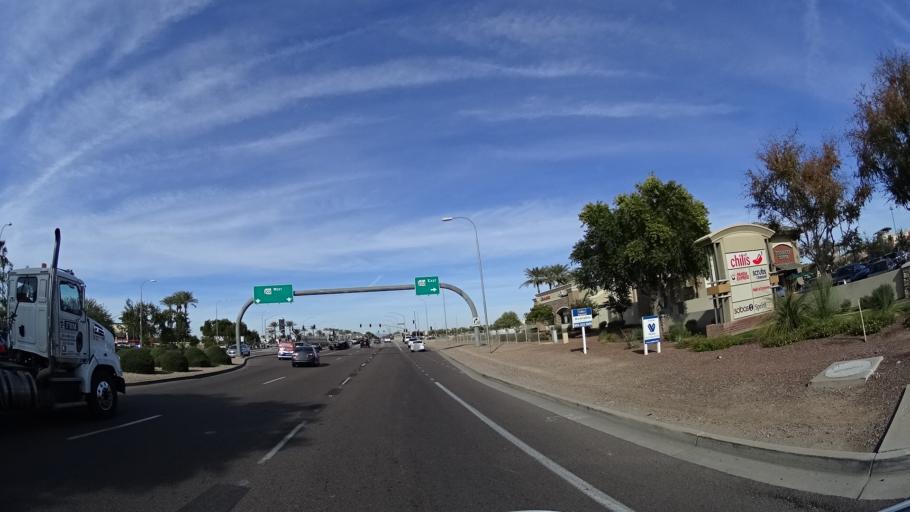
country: US
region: Arizona
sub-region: Maricopa County
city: Chandler
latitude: 33.2810
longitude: -111.7896
